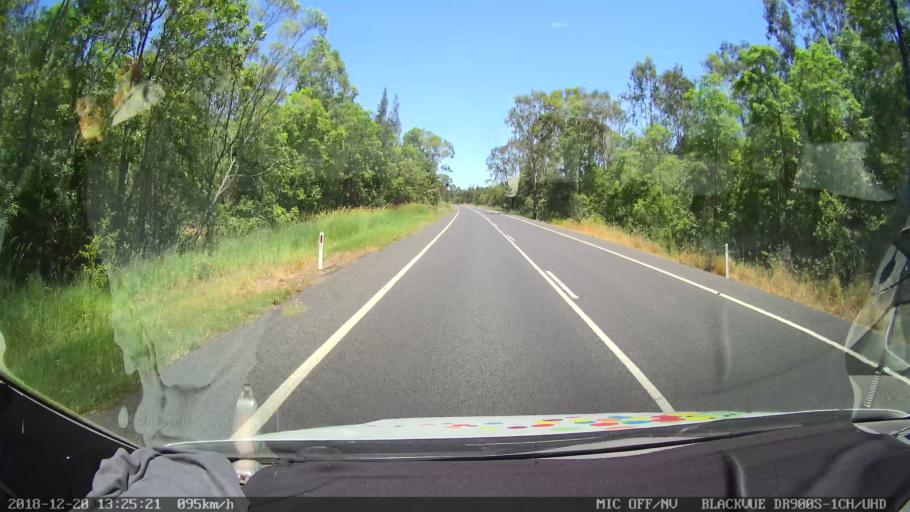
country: AU
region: New South Wales
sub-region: Richmond Valley
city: Casino
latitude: -29.1299
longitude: 152.9967
